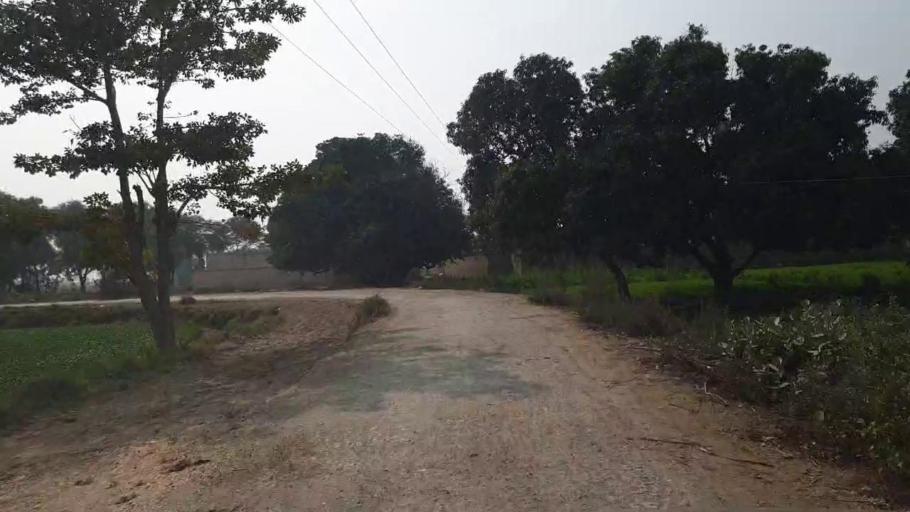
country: PK
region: Sindh
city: Bhit Shah
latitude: 25.8439
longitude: 68.5041
